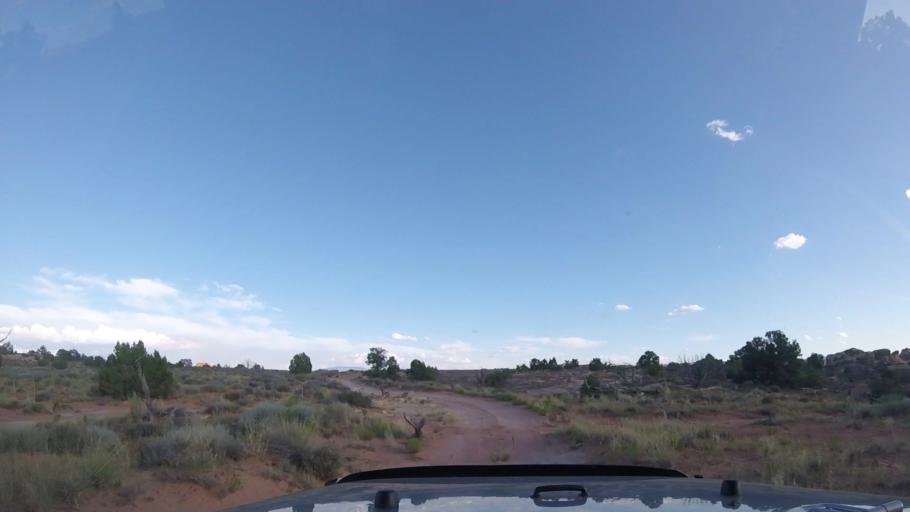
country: US
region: Utah
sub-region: Grand County
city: Moab
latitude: 38.2006
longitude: -109.7830
